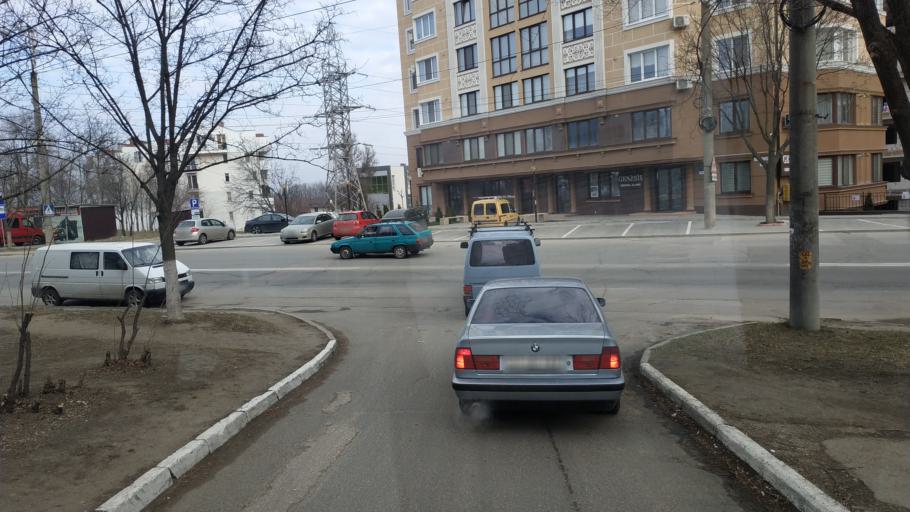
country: MD
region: Chisinau
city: Vatra
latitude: 47.0466
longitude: 28.7678
